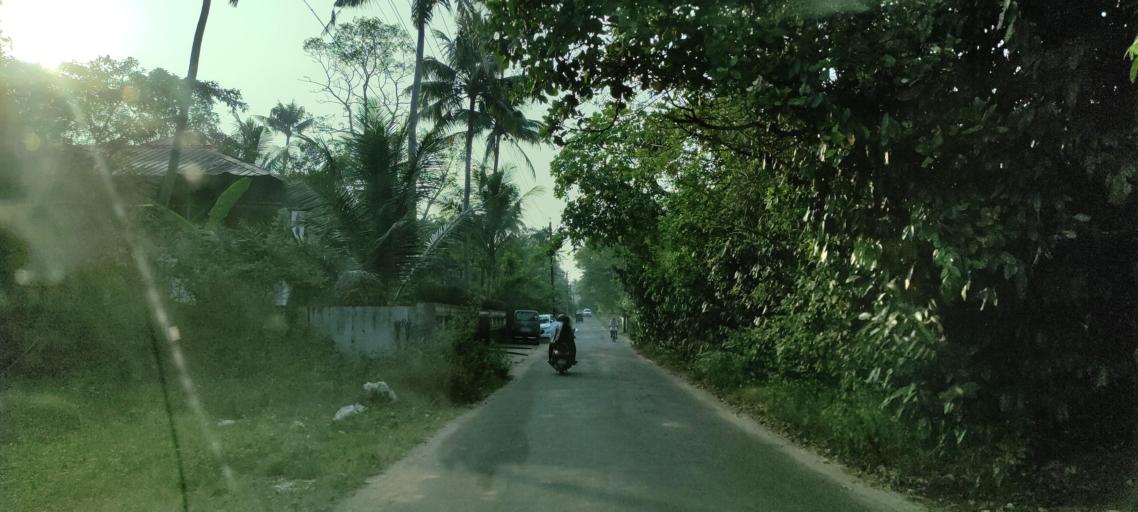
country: IN
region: Kerala
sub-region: Alappuzha
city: Shertallai
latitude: 9.6626
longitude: 76.3509
